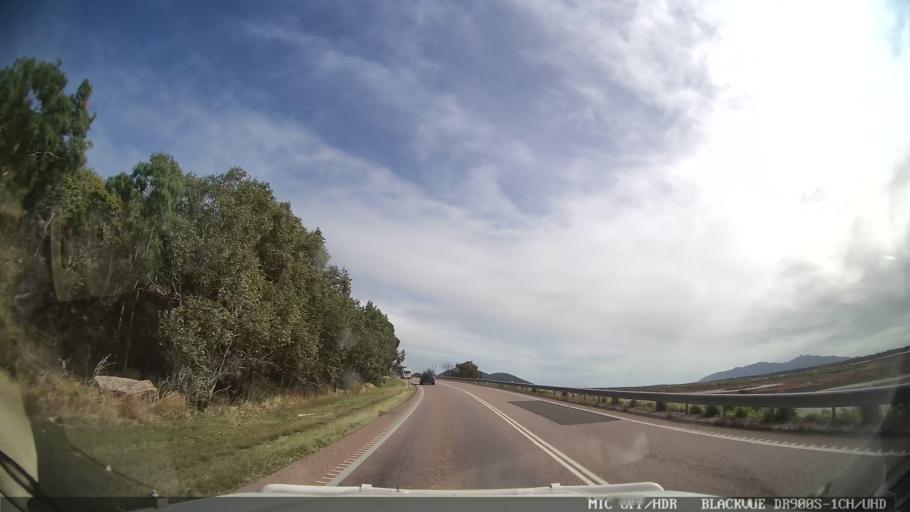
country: AU
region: Queensland
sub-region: Townsville
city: Townsville
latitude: -19.3947
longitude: 147.0200
